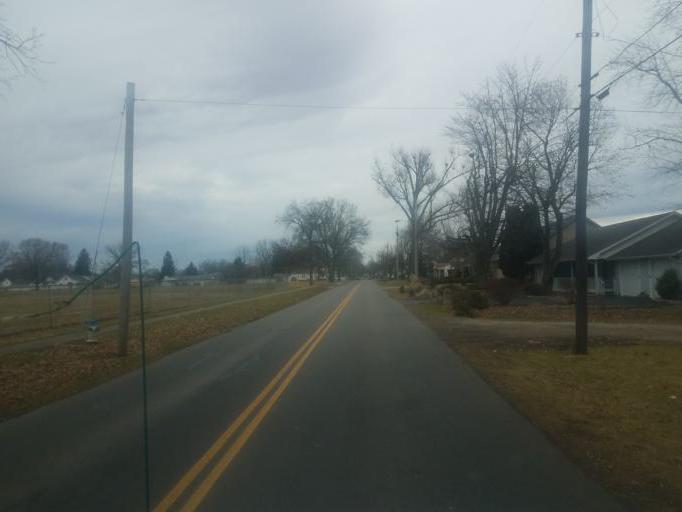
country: US
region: Ohio
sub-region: Marion County
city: Marion
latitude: 40.5835
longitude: -83.1024
